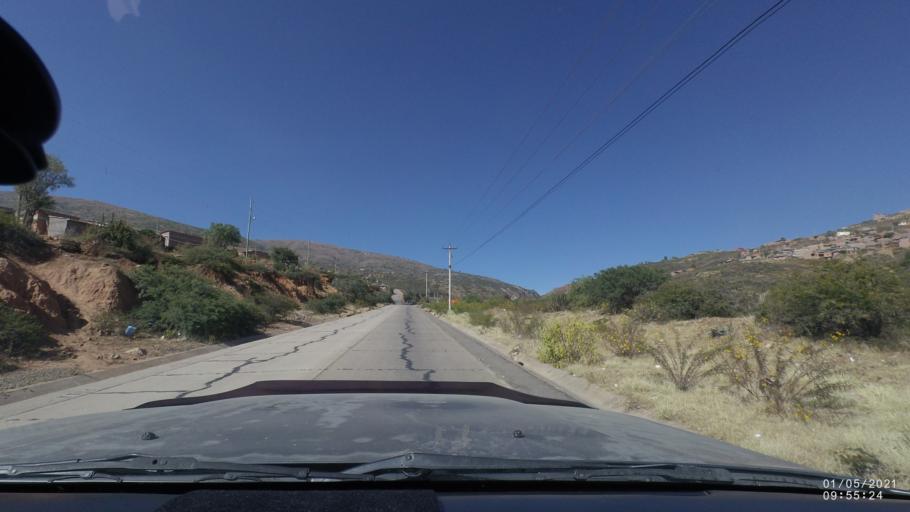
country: BO
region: Cochabamba
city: Cochabamba
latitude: -17.4986
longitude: -66.1720
